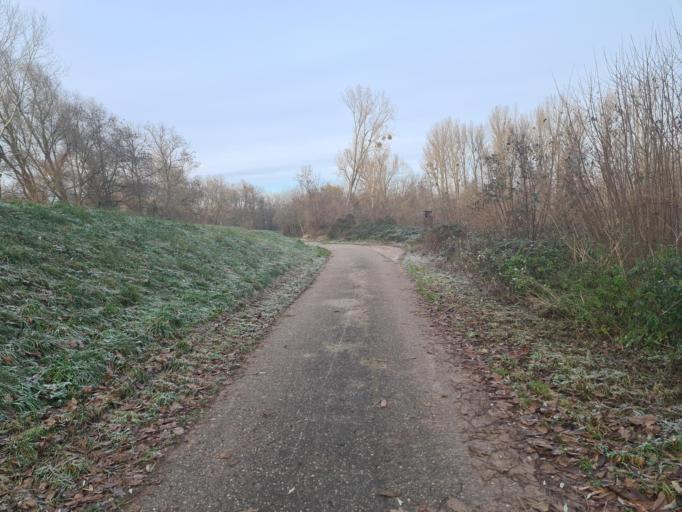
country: DE
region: Baden-Wuerttemberg
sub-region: Karlsruhe Region
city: Iffezheim
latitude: 48.8267
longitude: 8.1215
